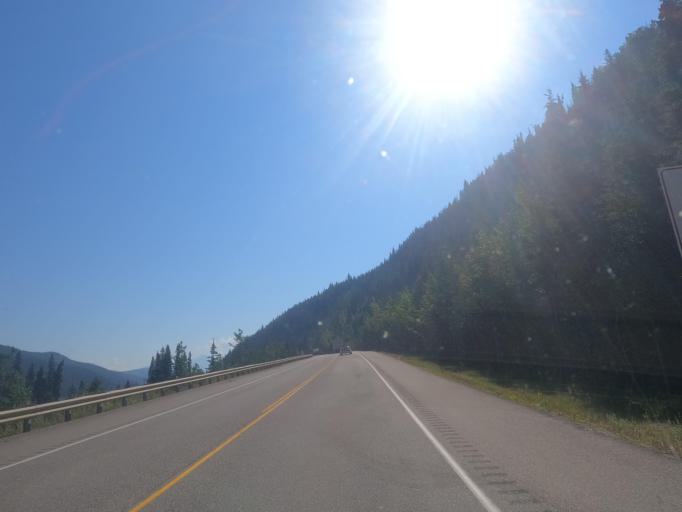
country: CA
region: Alberta
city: Jasper Park Lodge
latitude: 52.8778
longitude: -118.3437
